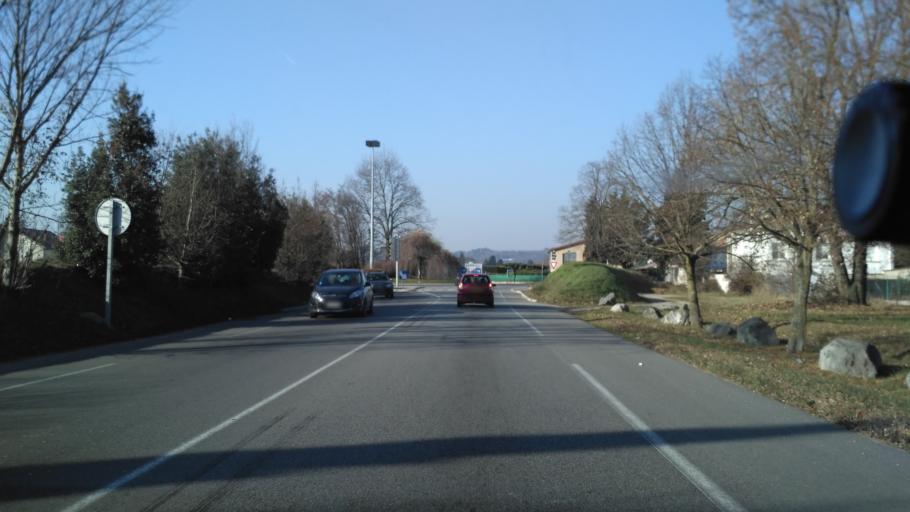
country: FR
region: Rhone-Alpes
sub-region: Departement de la Drome
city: Mours-Saint-Eusebe
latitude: 45.0608
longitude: 5.0523
